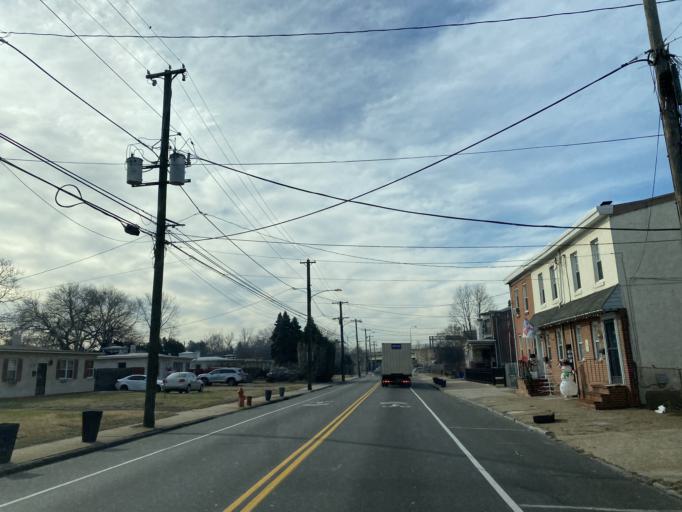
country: US
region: New Jersey
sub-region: Camden County
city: Pennsauken
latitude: 39.9920
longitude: -75.0839
